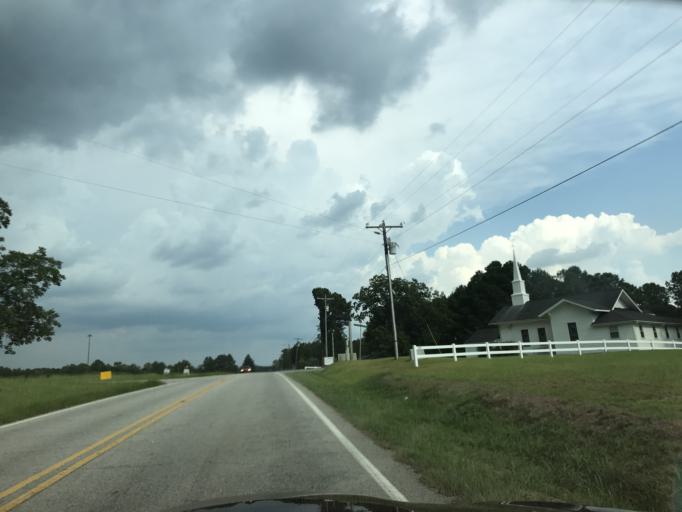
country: US
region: North Carolina
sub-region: Johnston County
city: Four Oaks
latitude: 35.5114
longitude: -78.5276
